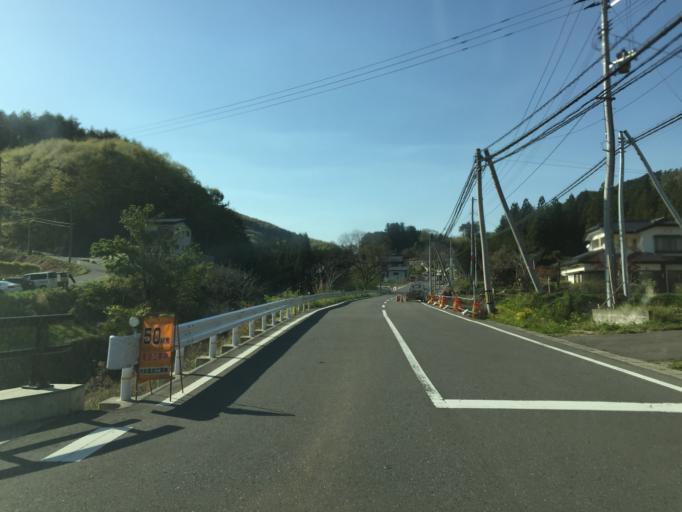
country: JP
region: Fukushima
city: Funehikimachi-funehiki
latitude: 37.5045
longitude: 140.7633
